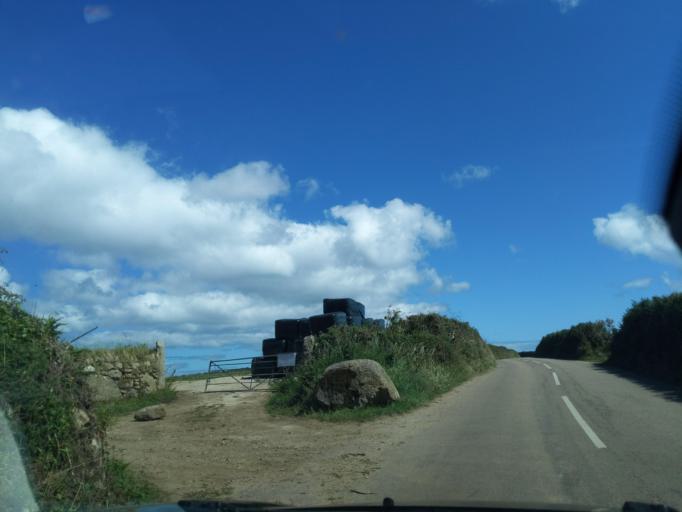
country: GB
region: England
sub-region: Cornwall
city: St. Buryan
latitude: 50.0545
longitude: -5.6537
